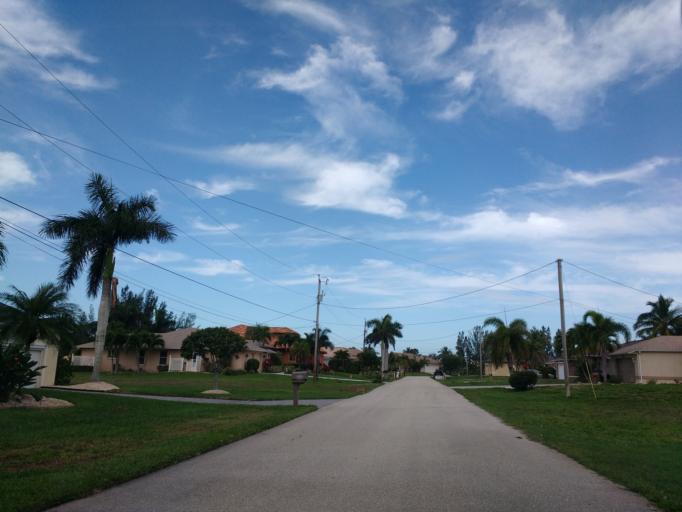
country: US
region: Florida
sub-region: Lee County
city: Cape Coral
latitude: 26.5853
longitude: -82.0287
